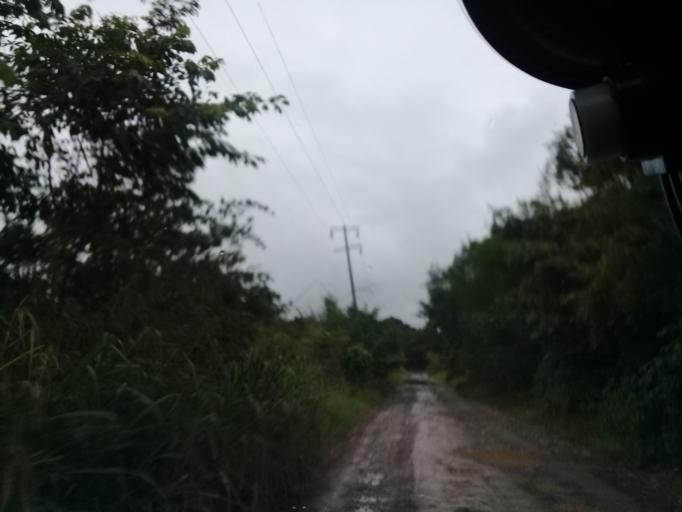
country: MX
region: Veracruz
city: Platon Sanchez
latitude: 21.2478
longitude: -98.3470
